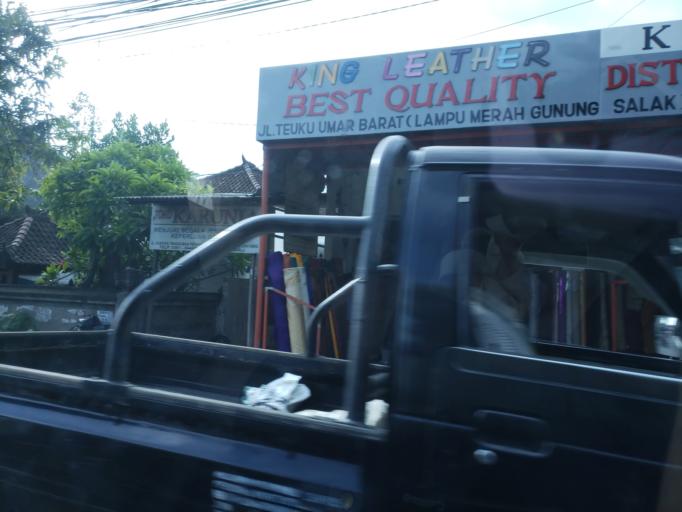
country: ID
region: Bali
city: Denpasar
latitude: -8.6733
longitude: 115.1813
